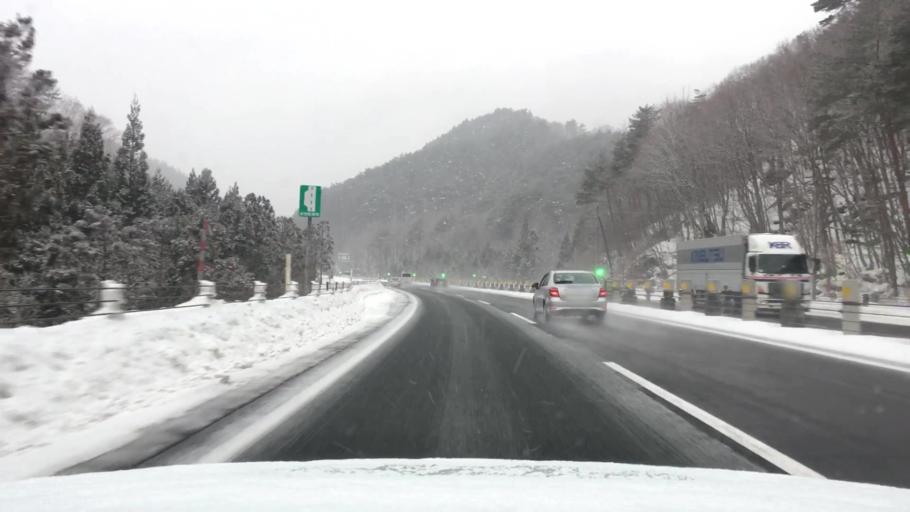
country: JP
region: Akita
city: Hanawa
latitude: 40.1160
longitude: 141.0303
